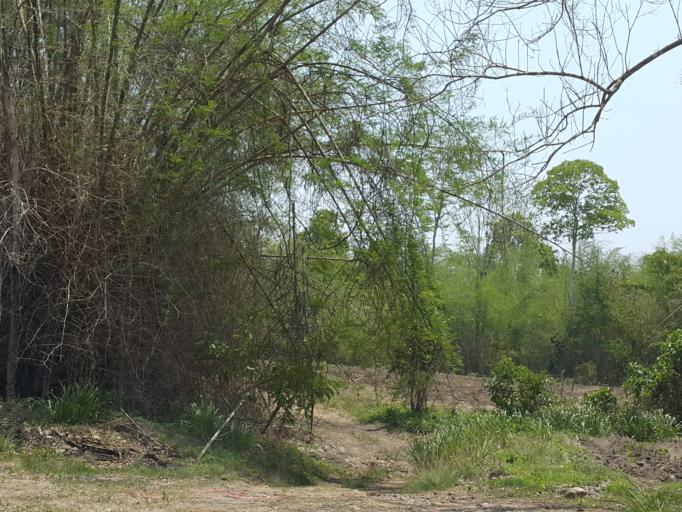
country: TH
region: Kanchanaburi
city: Sai Yok
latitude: 14.2173
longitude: 98.8767
